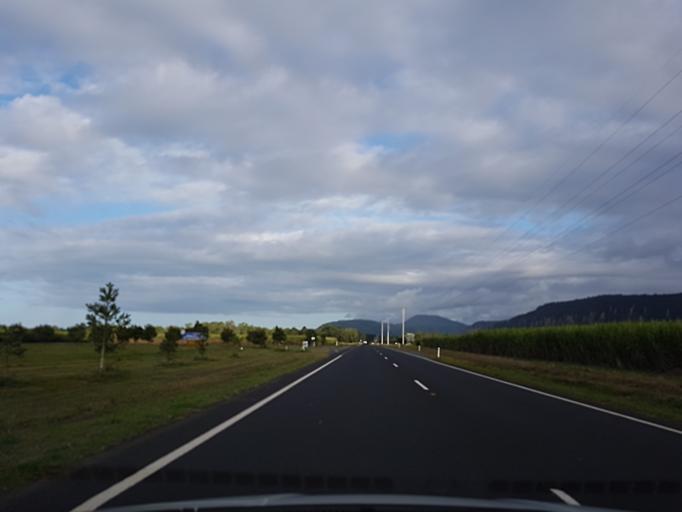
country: AU
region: Queensland
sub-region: Cairns
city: Port Douglas
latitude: -16.5160
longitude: 145.4471
